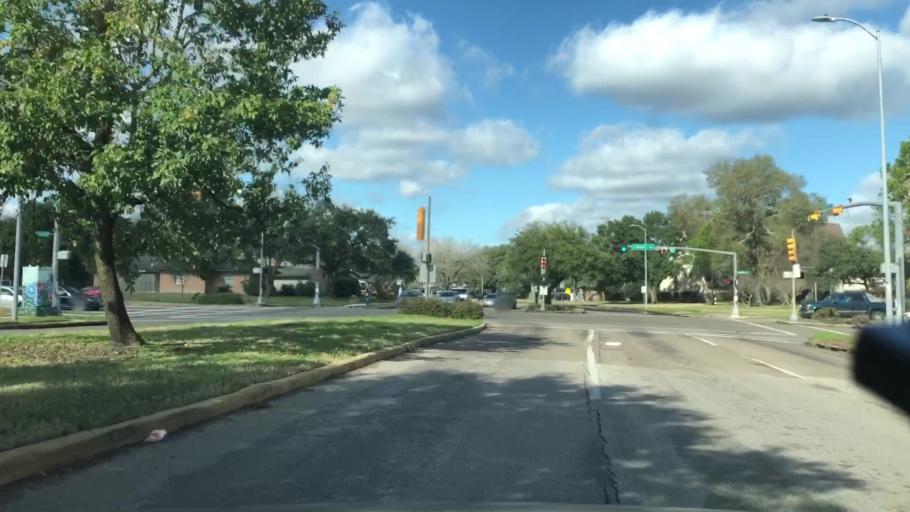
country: US
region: Texas
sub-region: Harris County
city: Bellaire
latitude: 29.6655
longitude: -95.4688
